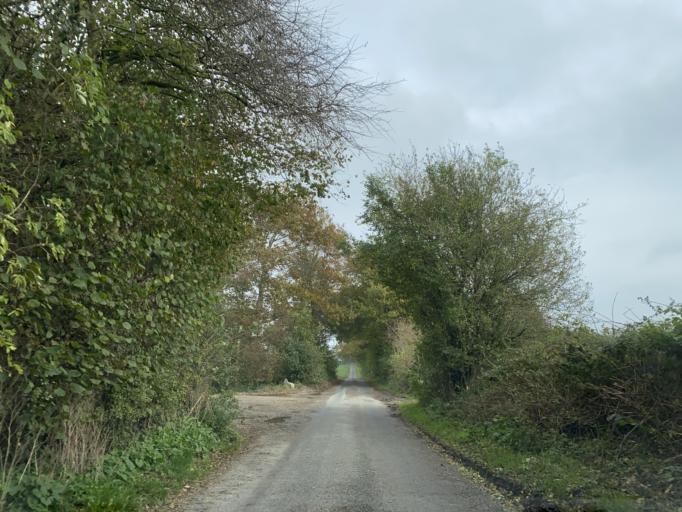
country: DK
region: South Denmark
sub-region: Aabenraa Kommune
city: Lojt Kirkeby
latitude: 55.1222
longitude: 9.4485
